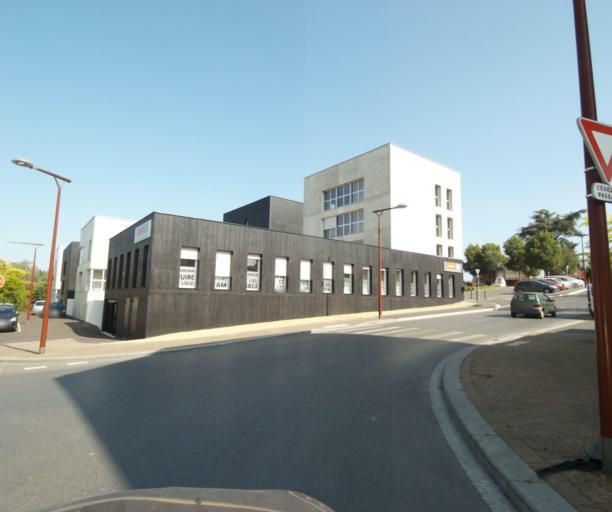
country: FR
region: Champagne-Ardenne
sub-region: Departement des Ardennes
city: Charleville-Mezieres
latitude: 49.7826
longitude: 4.7093
